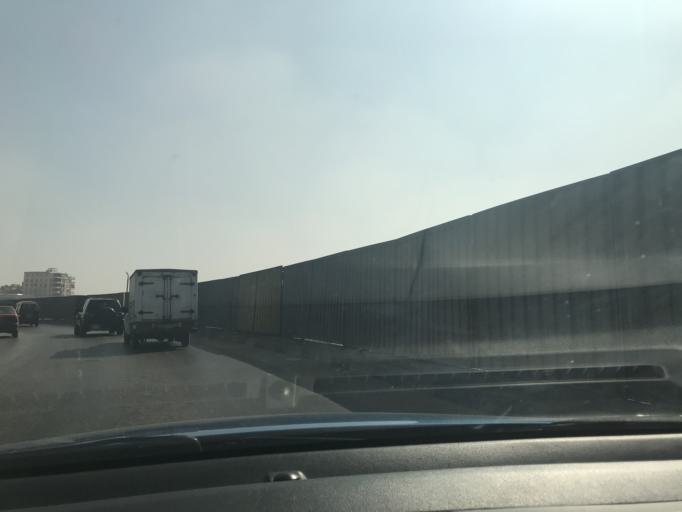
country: EG
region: Muhafazat al Qalyubiyah
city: Al Khankah
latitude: 30.1403
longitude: 31.4005
